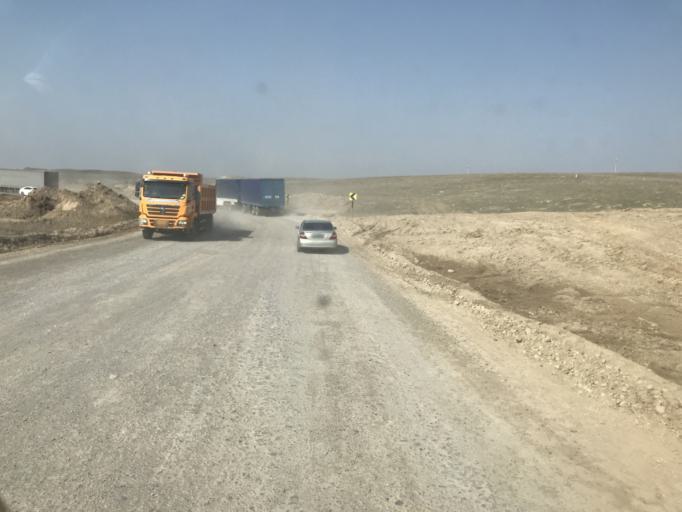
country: KG
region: Chuy
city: Bystrovka
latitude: 43.3207
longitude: 75.9994
